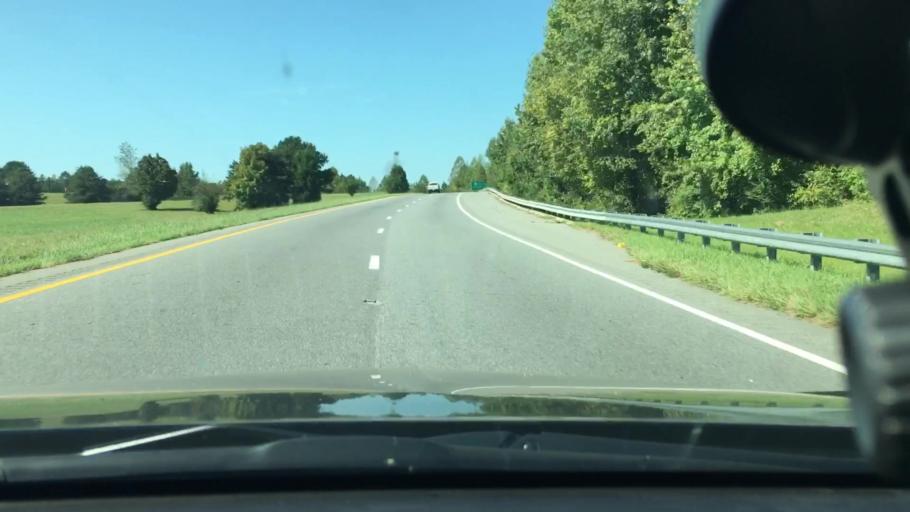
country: US
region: North Carolina
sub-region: Gaston County
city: Bessemer City
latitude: 35.2522
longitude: -81.2978
